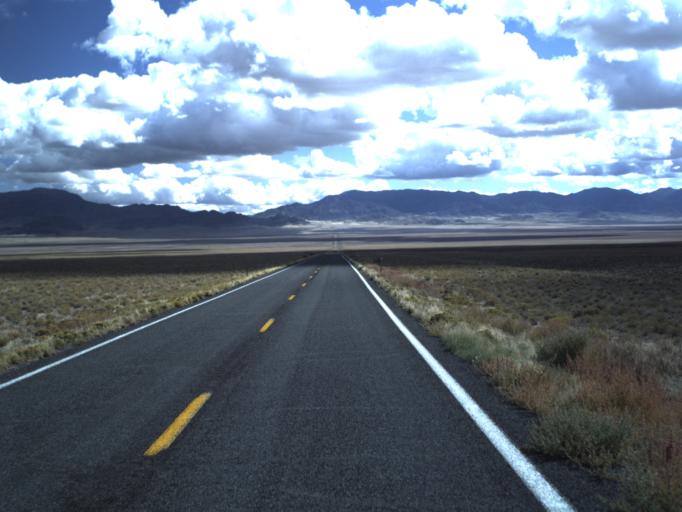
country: US
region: Utah
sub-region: Beaver County
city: Milford
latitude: 38.5713
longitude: -113.7876
